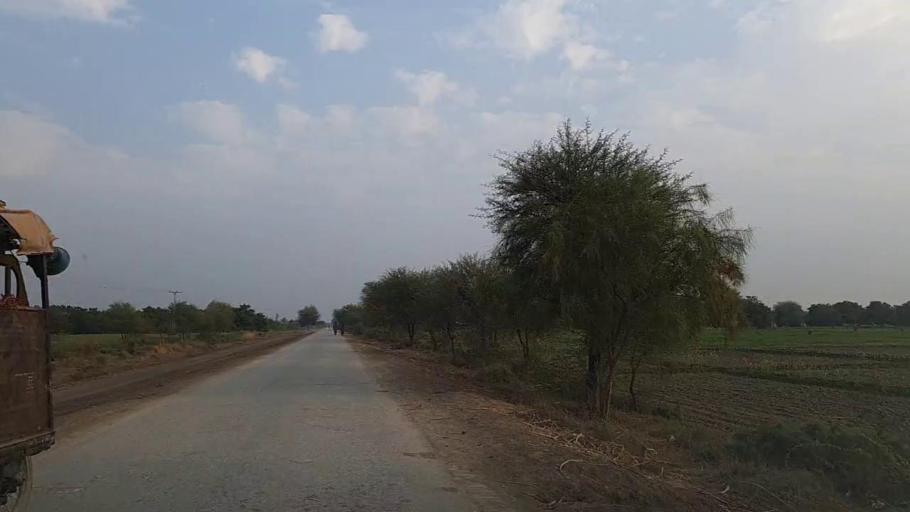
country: PK
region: Sindh
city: Mirwah Gorchani
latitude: 25.3013
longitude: 69.2196
